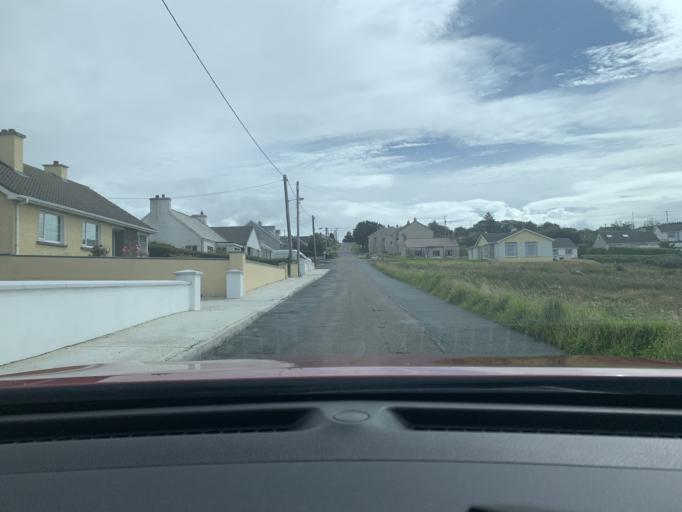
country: IE
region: Ulster
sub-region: County Donegal
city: Dungloe
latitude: 54.9463
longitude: -8.3590
